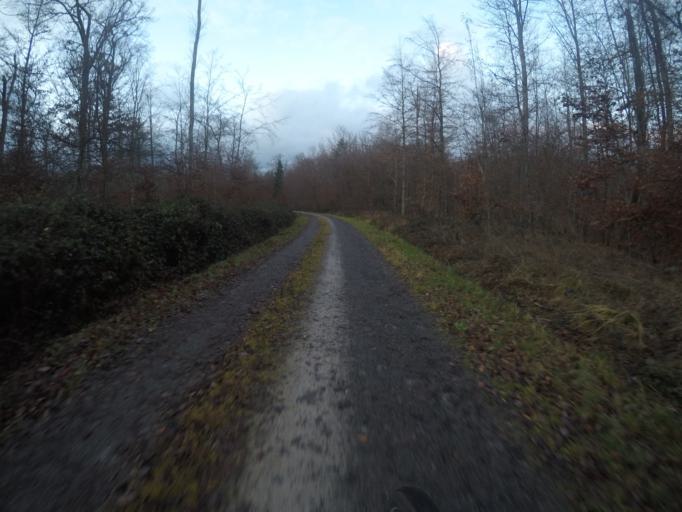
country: DE
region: Baden-Wuerttemberg
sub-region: Tuebingen Region
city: Dettenhausen
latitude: 48.5713
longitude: 9.1076
